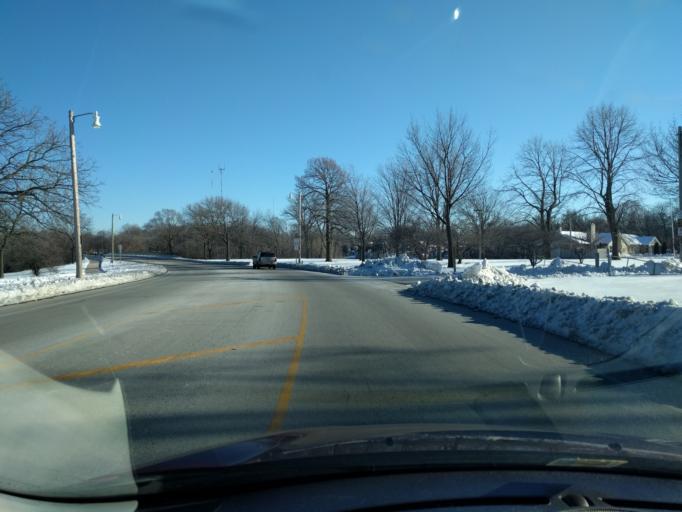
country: US
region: Wisconsin
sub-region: Milwaukee County
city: Whitefish Bay
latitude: 43.1047
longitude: -87.9276
